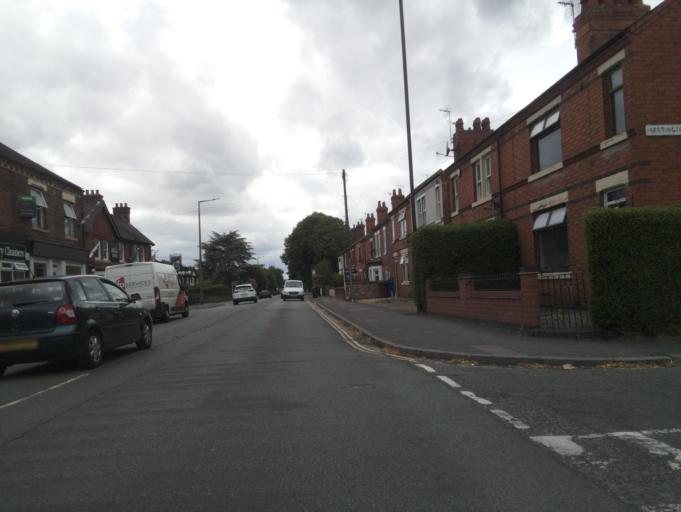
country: GB
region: England
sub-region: Derbyshire
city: Long Eaton
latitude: 52.8832
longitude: -1.2891
